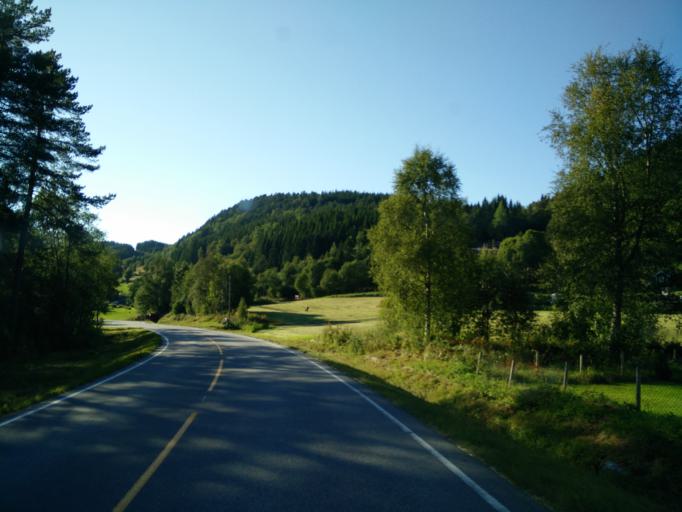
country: NO
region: More og Romsdal
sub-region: Halsa
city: Liaboen
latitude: 63.0868
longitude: 8.3907
